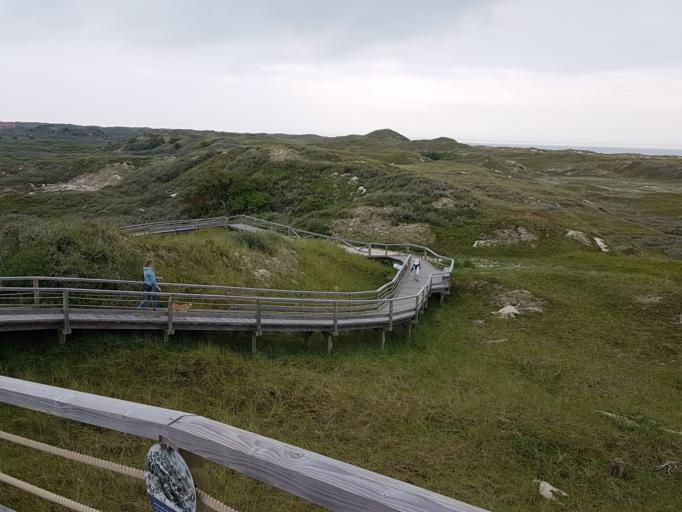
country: DE
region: Lower Saxony
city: Norderney
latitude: 53.7193
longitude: 7.1949
